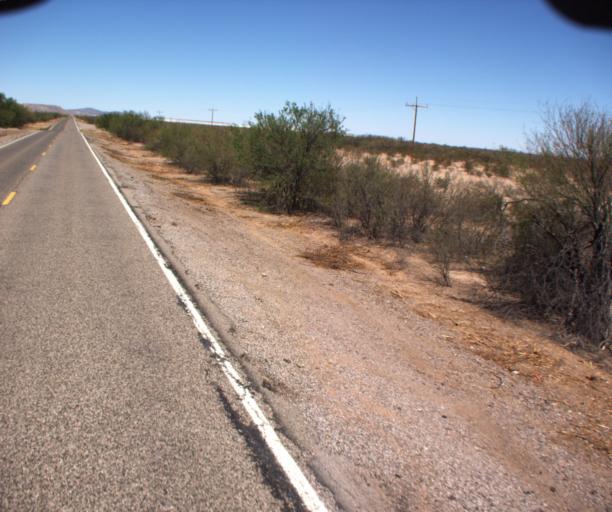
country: US
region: Arizona
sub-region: Pima County
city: Ajo
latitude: 32.3319
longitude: -112.7862
